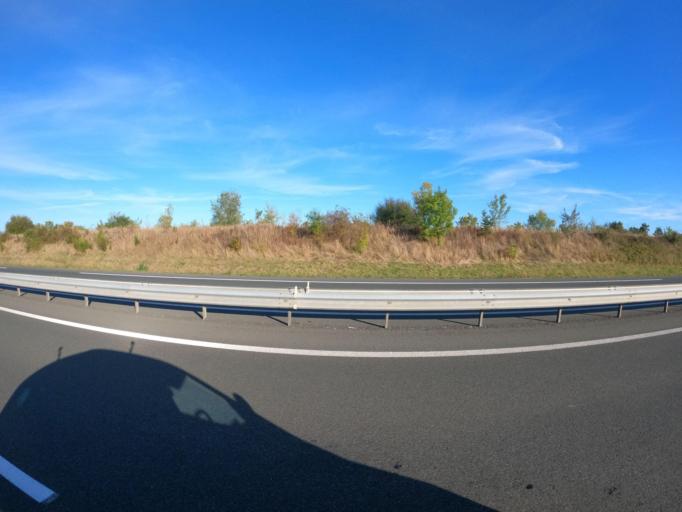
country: FR
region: Pays de la Loire
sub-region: Departement de Maine-et-Loire
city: Saint-Lambert-du-Lattay
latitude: 47.2885
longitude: -0.6152
